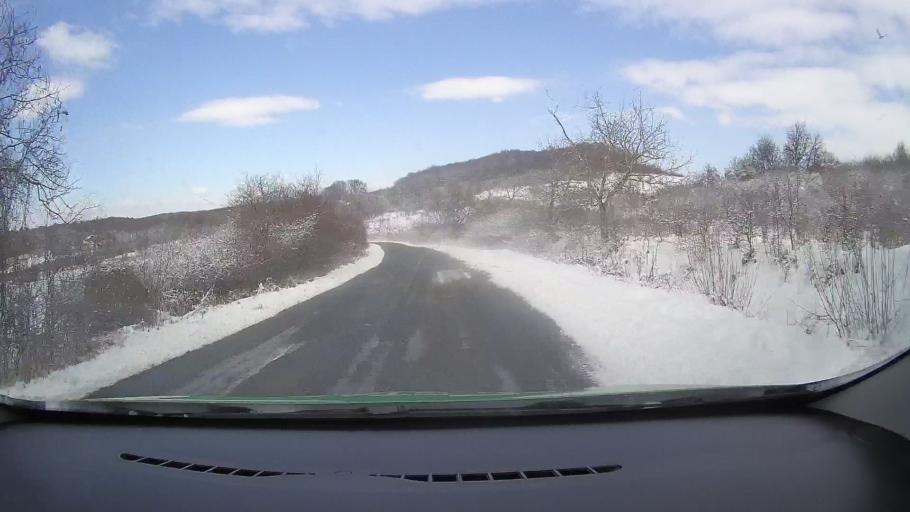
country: RO
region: Sibiu
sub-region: Comuna Mihaileni
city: Mihaileni
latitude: 46.0072
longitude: 24.4250
